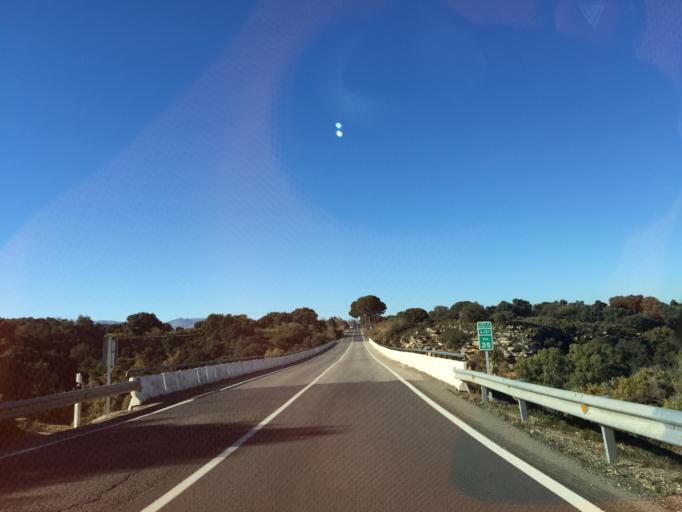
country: ES
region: Andalusia
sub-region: Provincia de Malaga
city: Arriate
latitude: 36.7926
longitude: -5.1066
